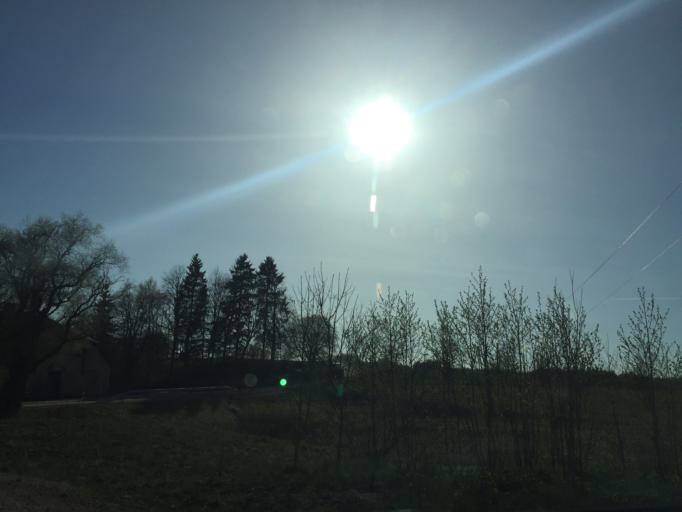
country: LV
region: Ergli
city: Ergli
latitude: 56.8693
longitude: 25.4760
